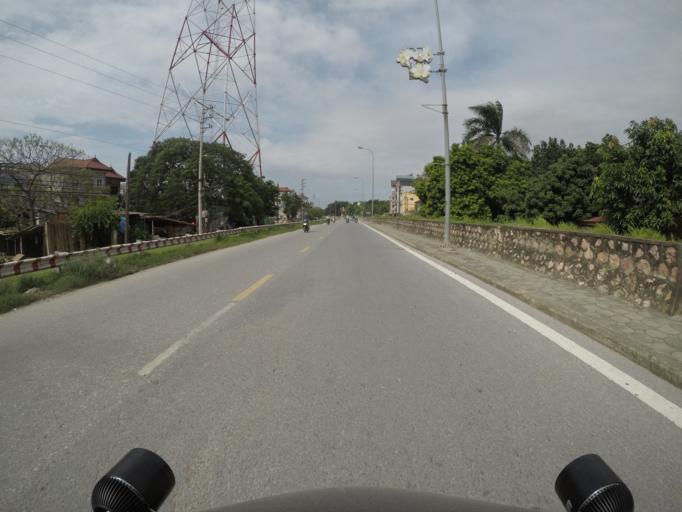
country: VN
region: Ha Noi
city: Tay Ho
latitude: 21.0941
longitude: 105.7768
